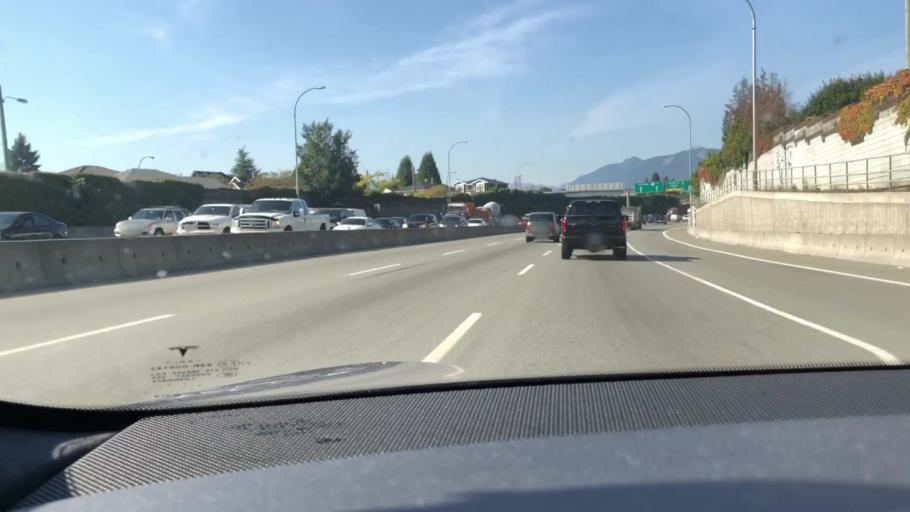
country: CA
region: British Columbia
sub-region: Fraser Valley Regional District
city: North Vancouver
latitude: 49.2743
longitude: -123.0305
